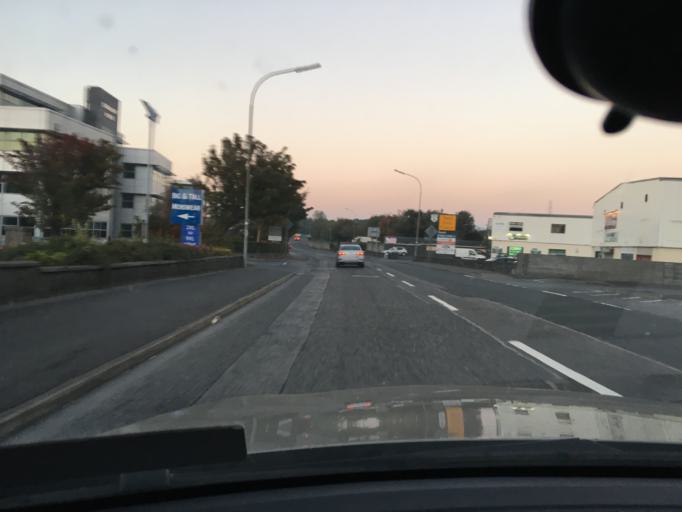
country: IE
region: Connaught
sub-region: County Galway
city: Gaillimh
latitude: 53.2832
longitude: -9.0364
